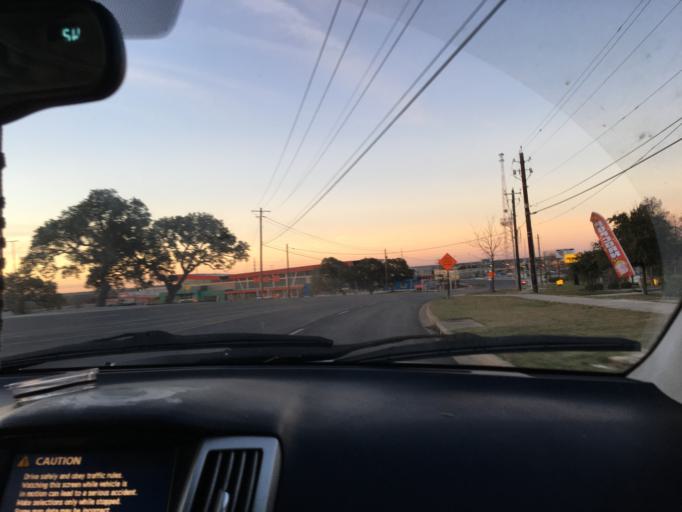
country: US
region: Texas
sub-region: Travis County
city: Onion Creek
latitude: 30.1713
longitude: -97.7860
